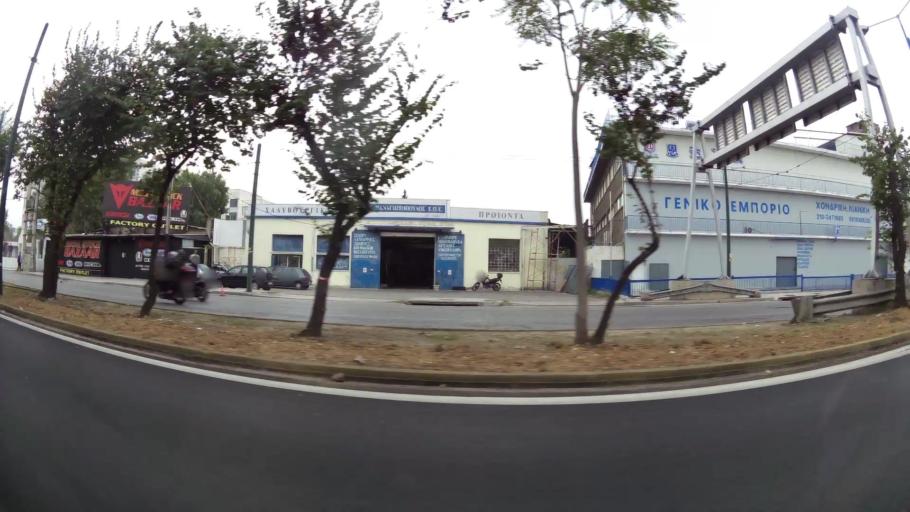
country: GR
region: Attica
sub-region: Nomarchia Athinas
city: Tavros
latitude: 37.9755
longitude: 23.7012
